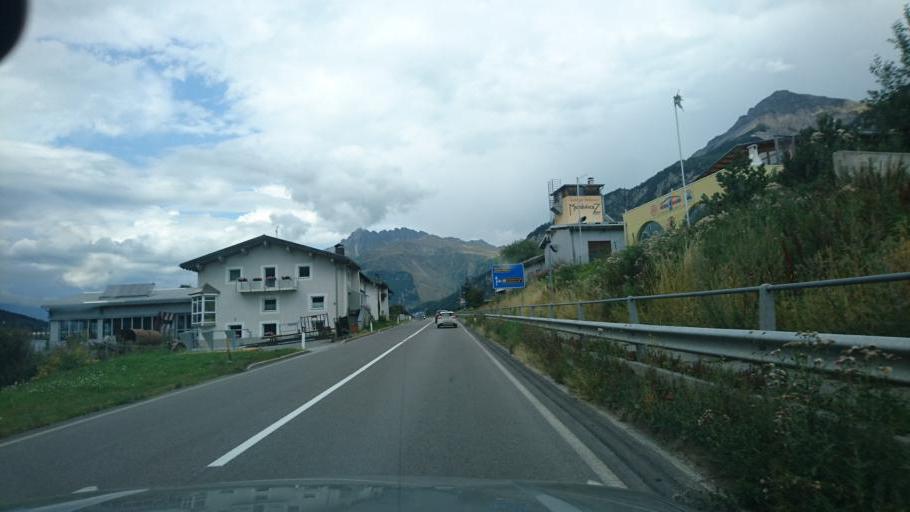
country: IT
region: Trentino-Alto Adige
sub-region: Bolzano
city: Curon Venosta
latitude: 46.7725
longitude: 10.5346
